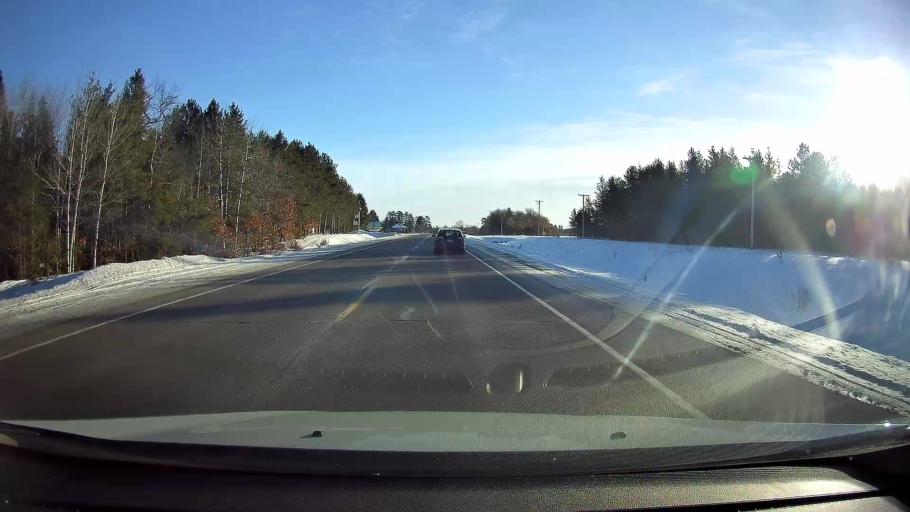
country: US
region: Wisconsin
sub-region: Washburn County
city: Spooner
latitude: 45.9101
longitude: -91.7712
